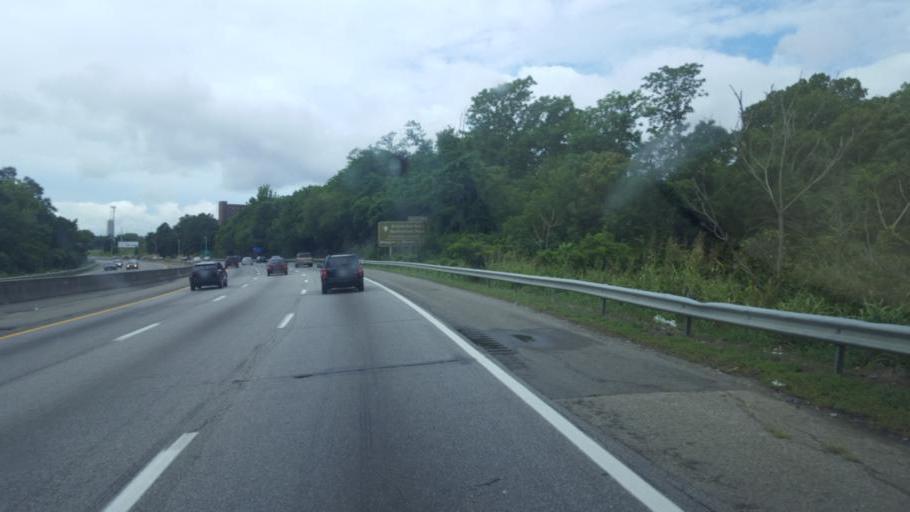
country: US
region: Virginia
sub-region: Henrico County
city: East Highland Park
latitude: 37.5588
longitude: -77.4208
